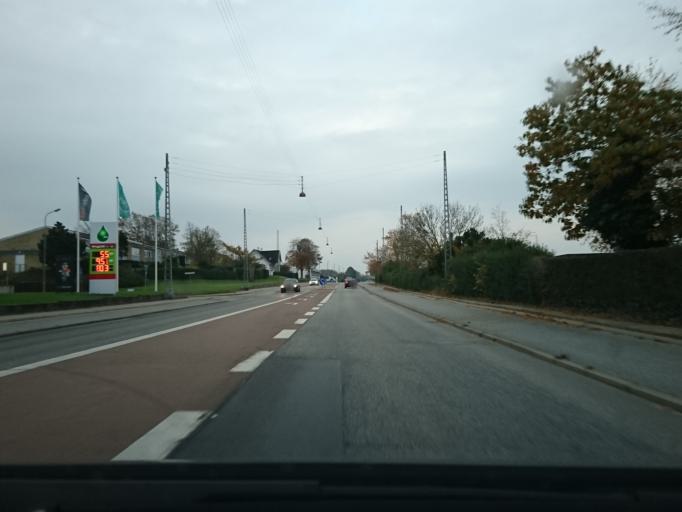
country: DK
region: North Denmark
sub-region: Alborg Kommune
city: Aalborg
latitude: 57.0238
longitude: 9.9269
